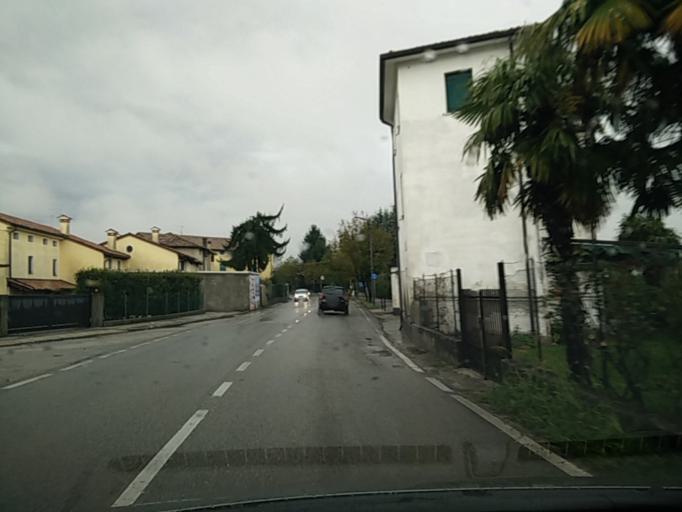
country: IT
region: Veneto
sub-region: Provincia di Vicenza
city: Rosa
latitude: 45.7216
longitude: 11.7750
